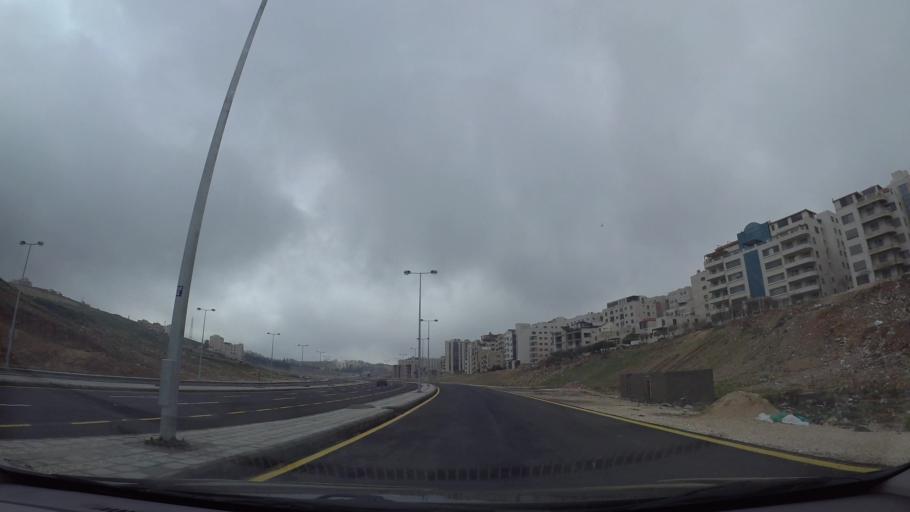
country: JO
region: Amman
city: Al Bunayyat ash Shamaliyah
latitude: 31.9343
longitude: 35.8668
